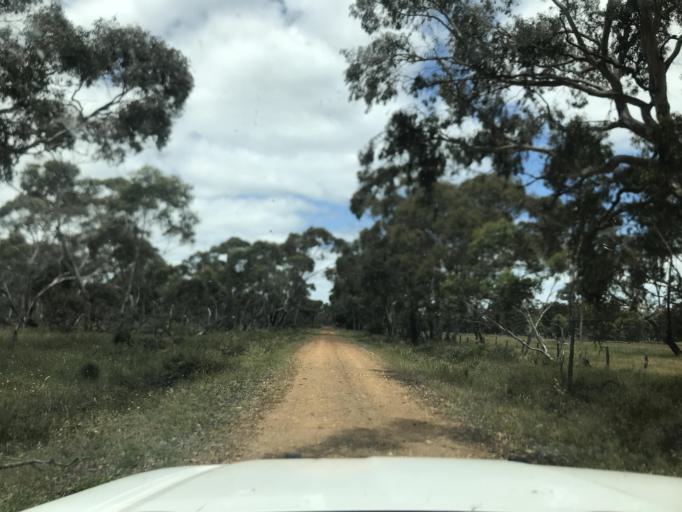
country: AU
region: South Australia
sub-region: Wattle Range
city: Penola
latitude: -37.3595
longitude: 141.1101
